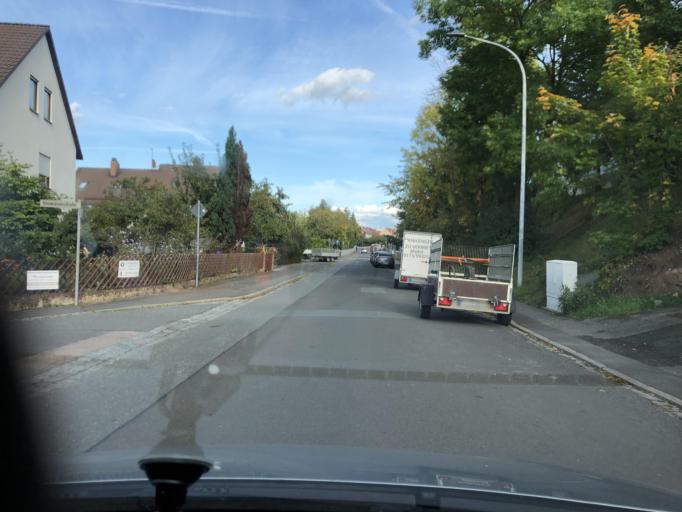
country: DE
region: Bavaria
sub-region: Regierungsbezirk Mittelfranken
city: Cadolzburg
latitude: 49.4626
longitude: 10.8525
